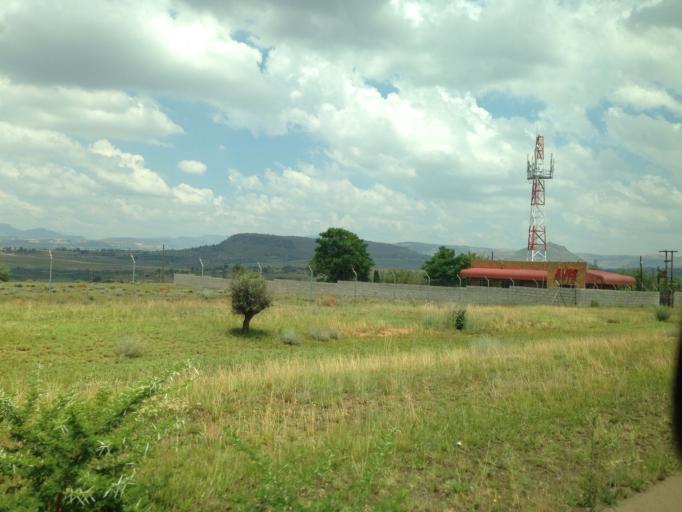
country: LS
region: Maseru
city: Maseru
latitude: -29.4576
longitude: 27.5600
